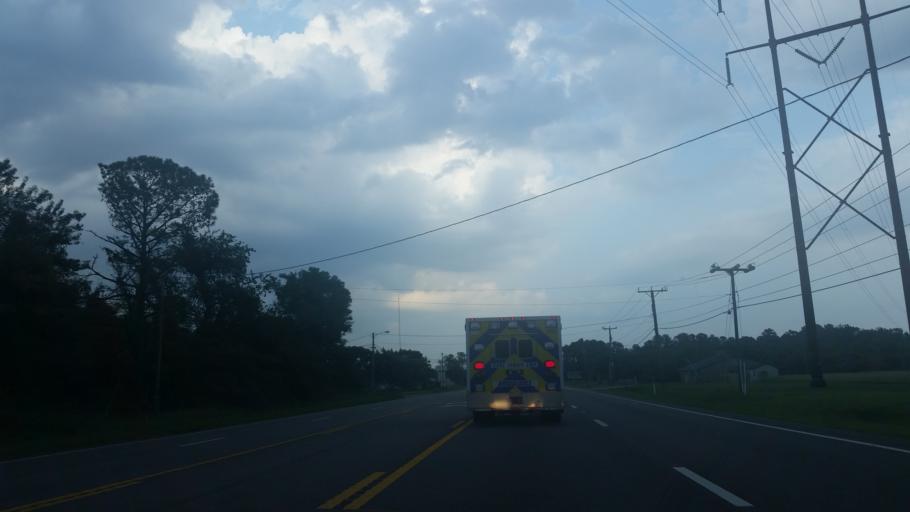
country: US
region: North Carolina
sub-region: Dare County
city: Southern Shores
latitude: 36.1475
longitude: -75.8500
